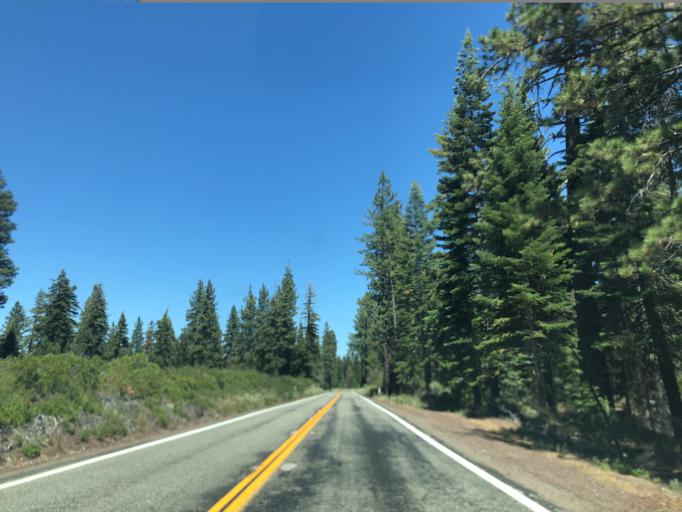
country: US
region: California
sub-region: Shasta County
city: Burney
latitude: 40.6135
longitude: -121.5064
